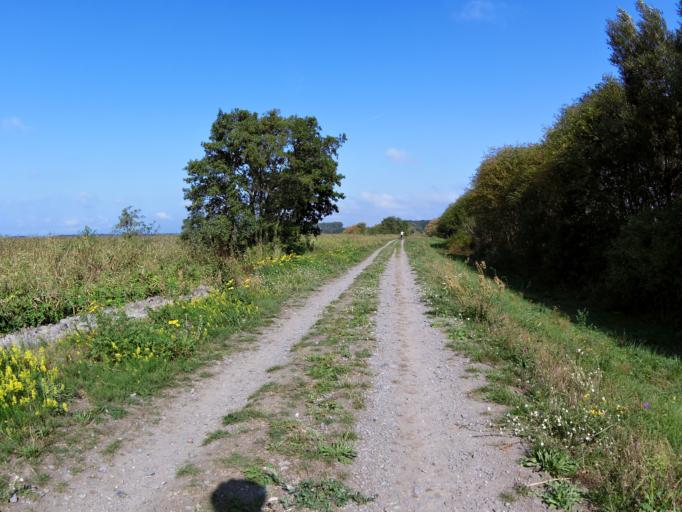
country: DE
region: Mecklenburg-Vorpommern
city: Loddin
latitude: 53.9894
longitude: 14.0480
